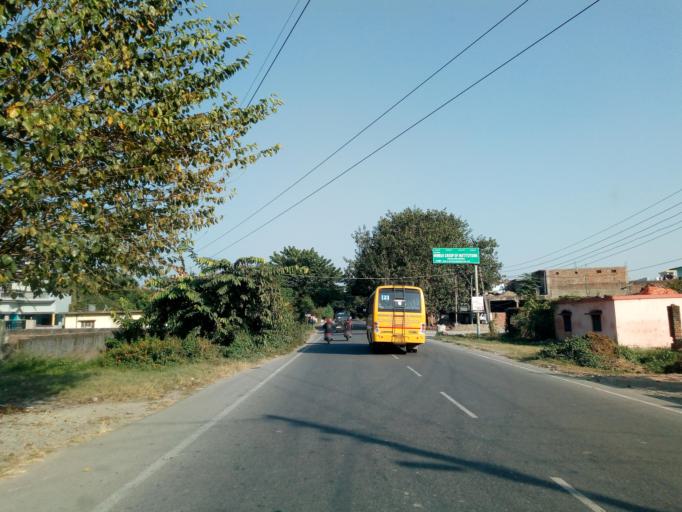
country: IN
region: Uttarakhand
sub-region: Dehradun
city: Dehradun
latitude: 30.3457
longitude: 77.9015
